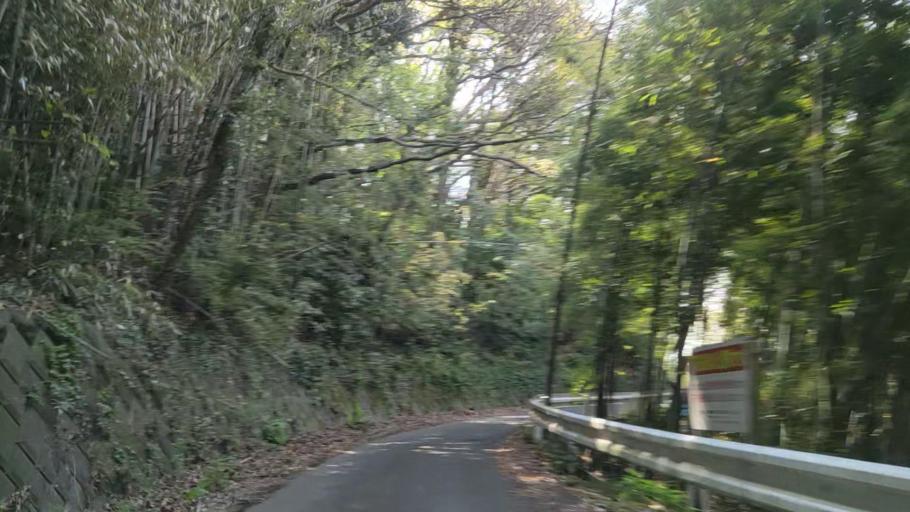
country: JP
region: Kanagawa
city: Ninomiya
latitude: 35.3264
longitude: 139.2674
